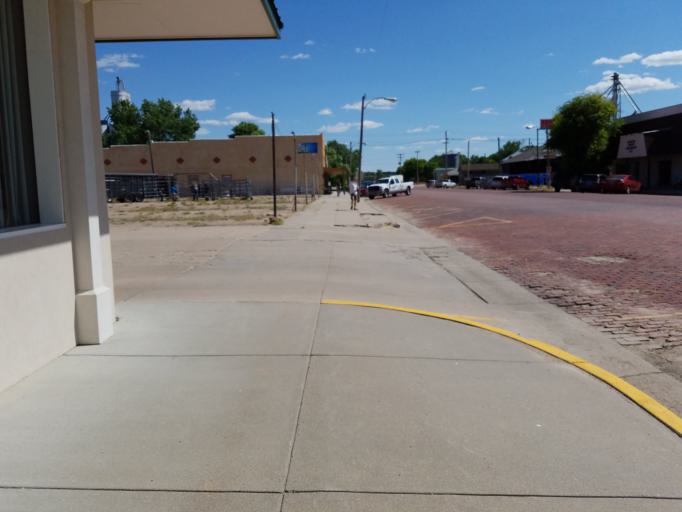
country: US
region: Kansas
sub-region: Decatur County
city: Oberlin
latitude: 39.8187
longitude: -100.5288
